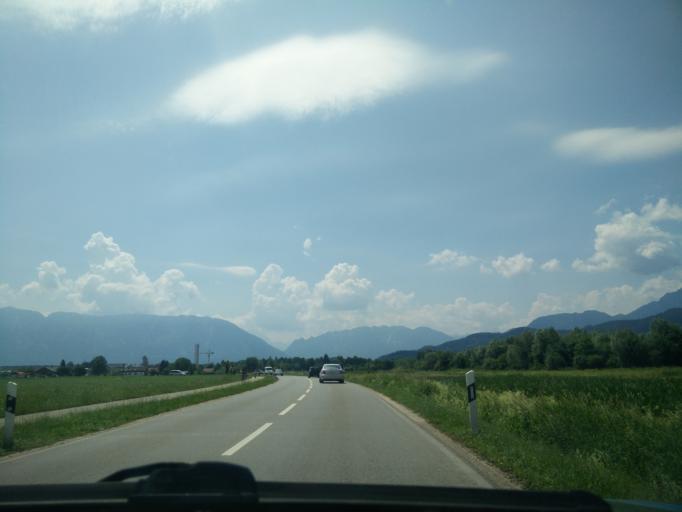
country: DE
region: Bavaria
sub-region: Upper Bavaria
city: Ainring
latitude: 47.8262
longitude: 12.9534
